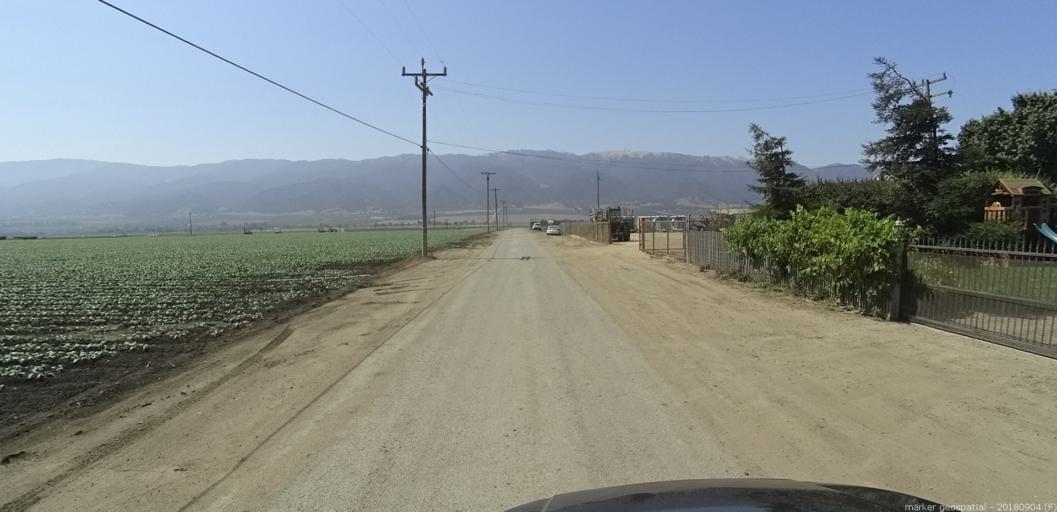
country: US
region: California
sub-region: Monterey County
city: Gonzales
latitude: 36.5090
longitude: -121.4746
